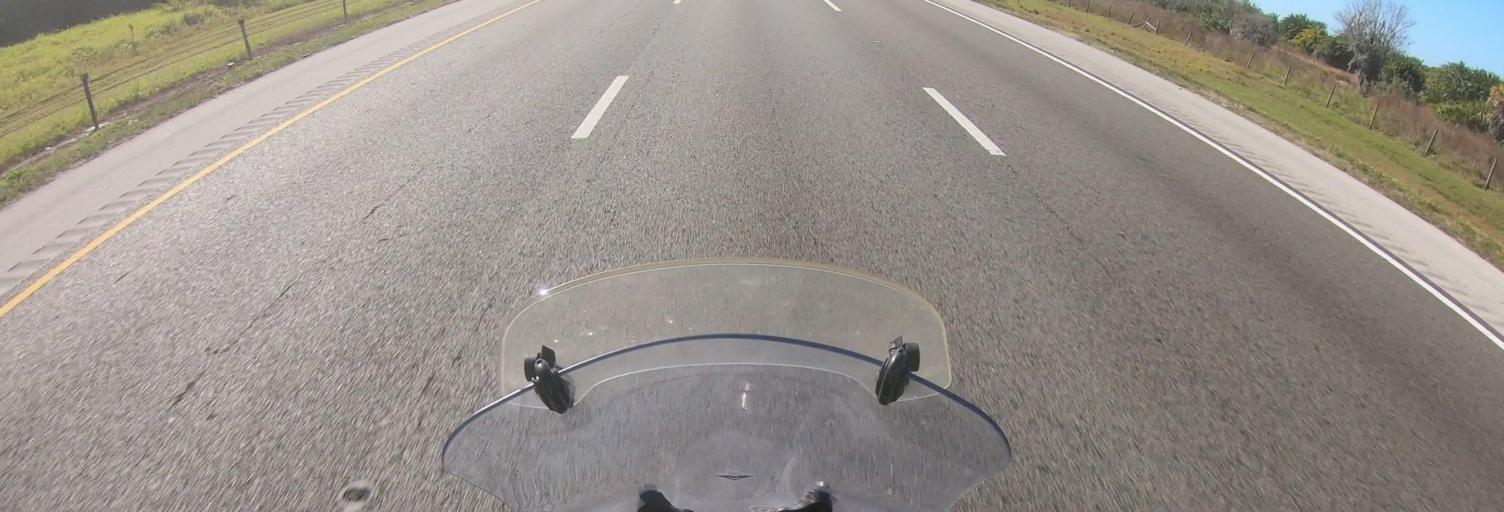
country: US
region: Florida
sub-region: Manatee County
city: Ellenton
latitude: 27.5647
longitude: -82.5163
